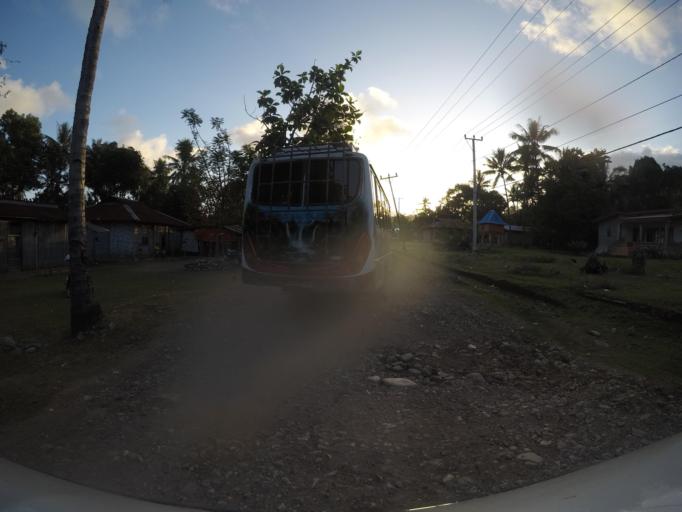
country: TL
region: Baucau
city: Venilale
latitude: -8.7490
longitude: 126.7034
